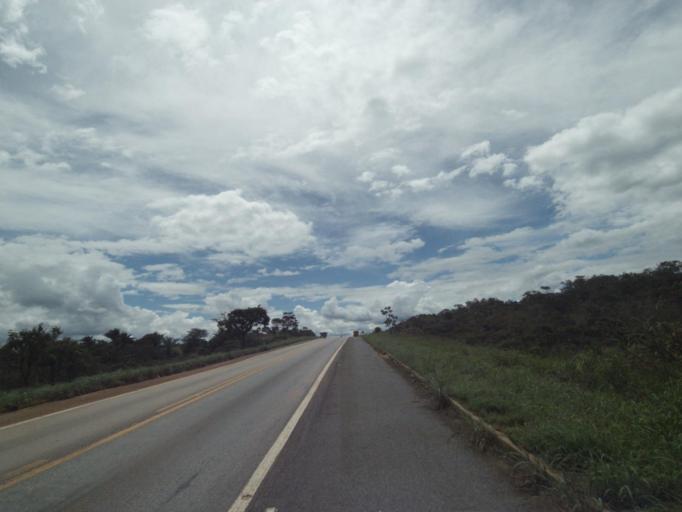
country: BR
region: Goias
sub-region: Pirenopolis
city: Pirenopolis
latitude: -15.7761
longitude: -48.5028
